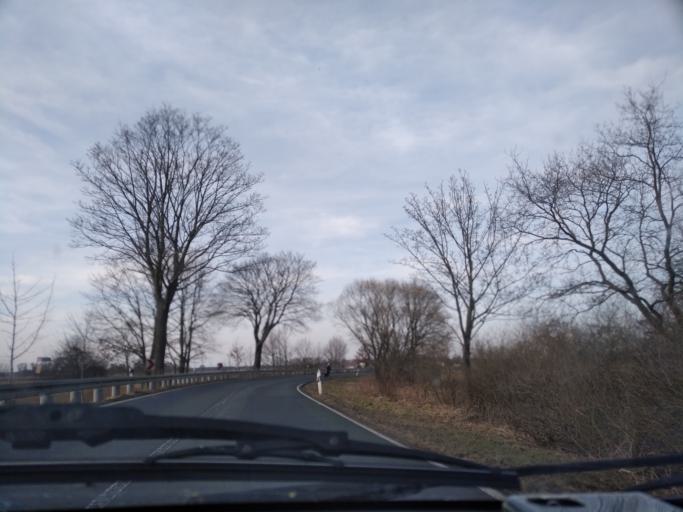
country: DE
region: Saxony-Anhalt
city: Holzdorf
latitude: 51.8109
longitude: 13.1640
